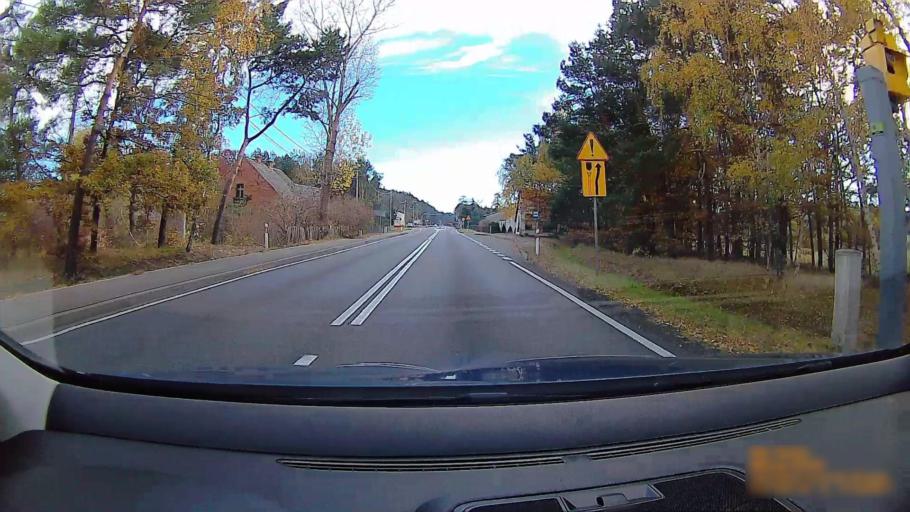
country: PL
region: Greater Poland Voivodeship
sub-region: Powiat ostrzeszowski
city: Ostrzeszow
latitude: 51.4836
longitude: 17.8751
